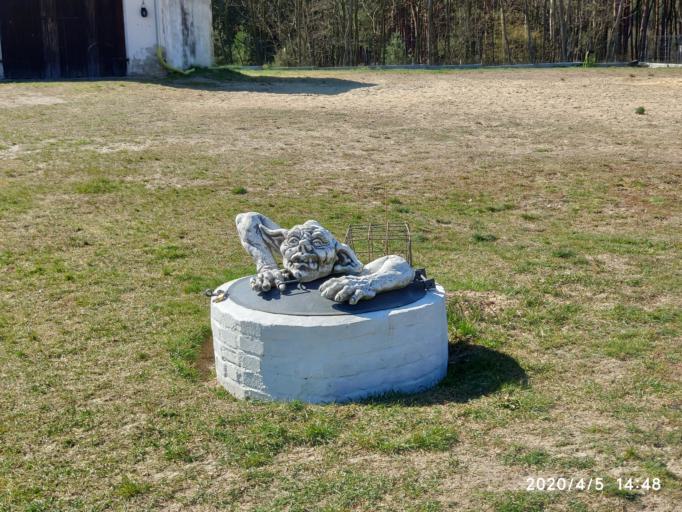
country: PL
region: Lubusz
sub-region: Powiat krosnienski
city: Dabie
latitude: 52.0321
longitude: 15.2492
